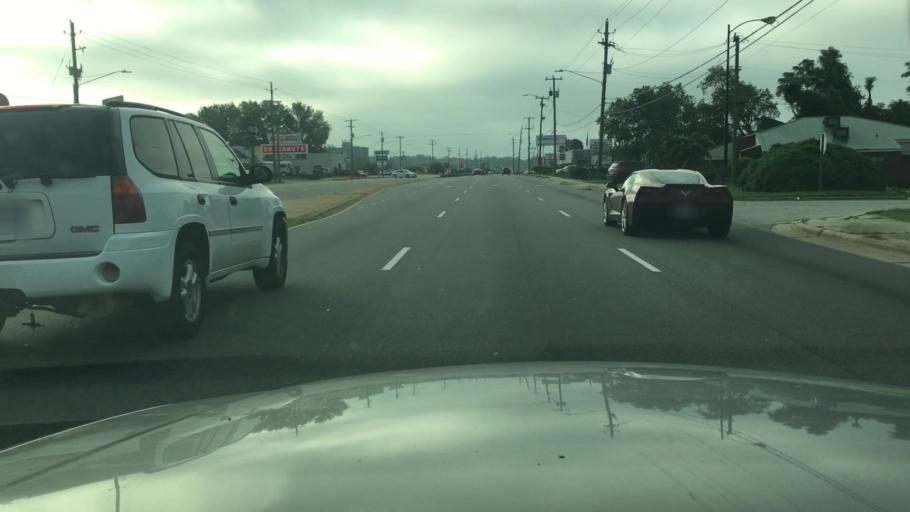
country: US
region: North Carolina
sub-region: Cumberland County
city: Fayetteville
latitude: 35.0769
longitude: -78.9358
